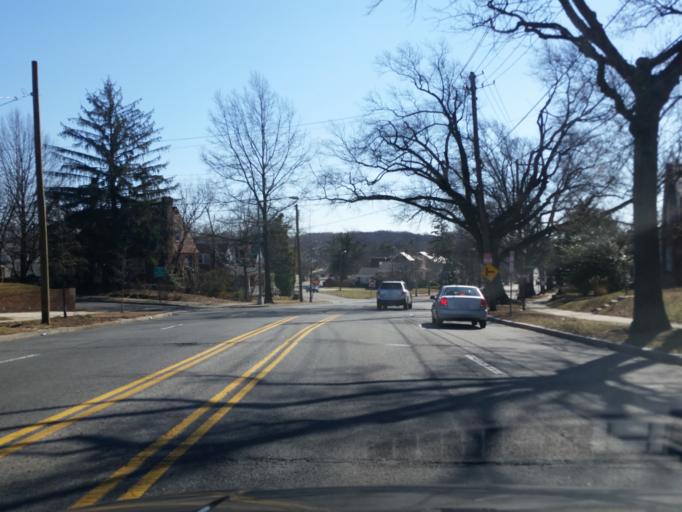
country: US
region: Maryland
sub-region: Montgomery County
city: Takoma Park
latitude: 38.9600
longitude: -77.0092
